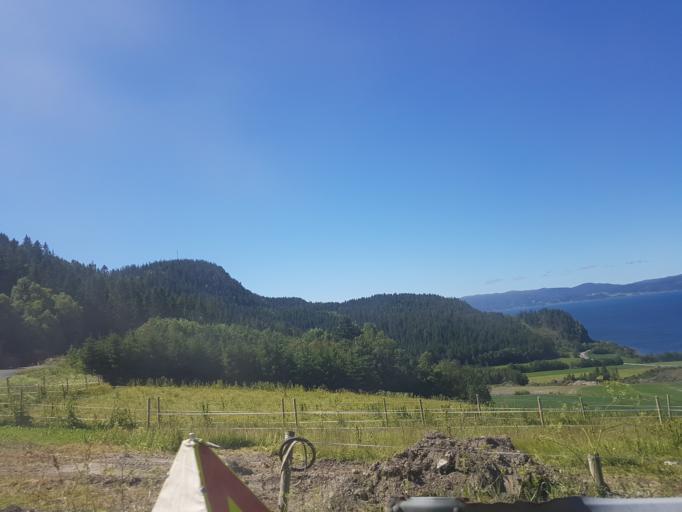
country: NO
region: Sor-Trondelag
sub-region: Skaun
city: Borsa
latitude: 63.4418
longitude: 10.1950
